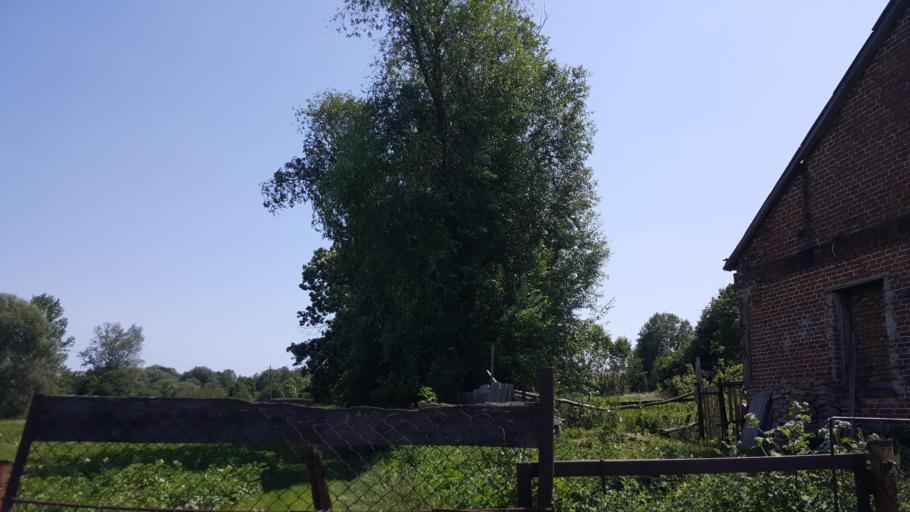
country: BY
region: Brest
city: Vysokaye
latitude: 52.3659
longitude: 23.3987
